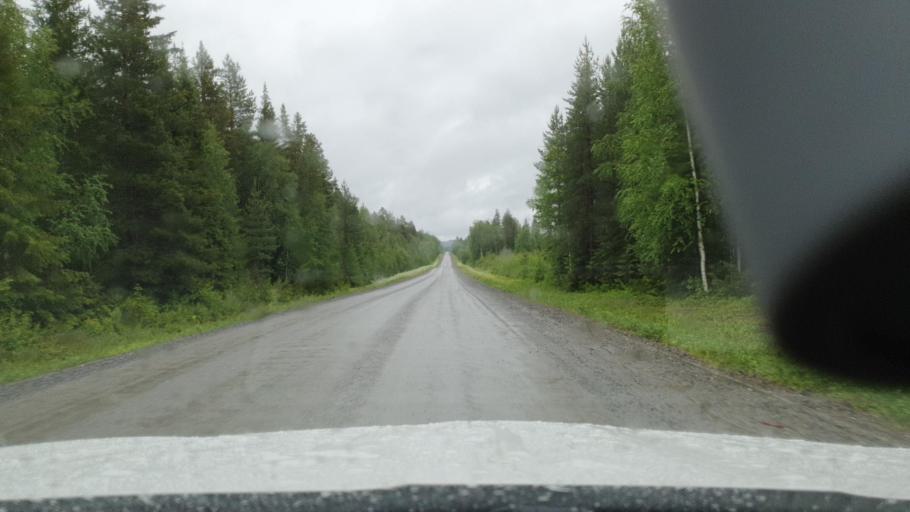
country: SE
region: Vaesterbotten
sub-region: Skelleftea Kommun
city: Burtraesk
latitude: 64.3787
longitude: 20.3465
